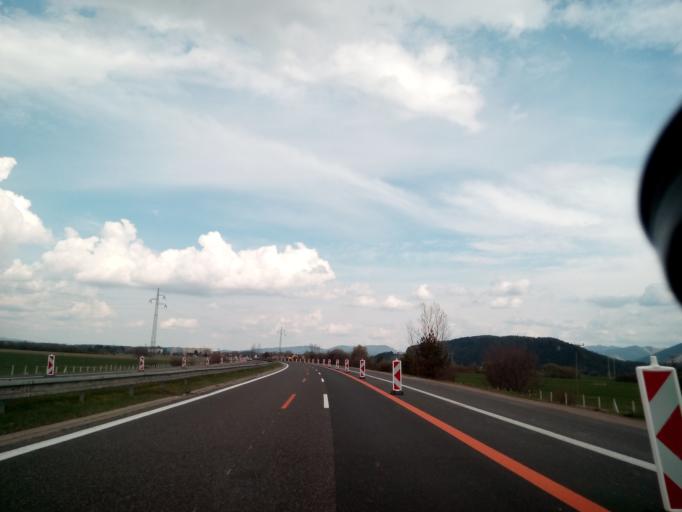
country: SK
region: Zilinsky
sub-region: Okres Zilina
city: Liptovsky Hradok
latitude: 49.0536
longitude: 19.7114
